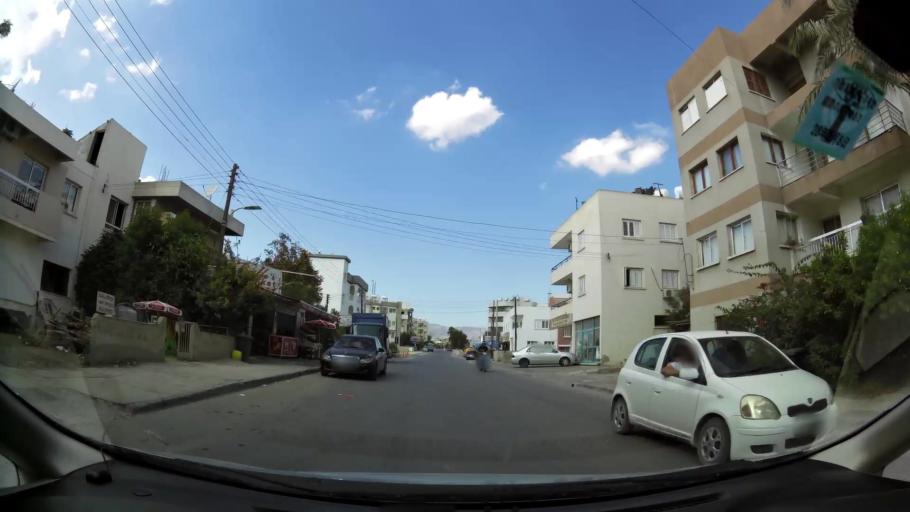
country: CY
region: Lefkosia
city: Nicosia
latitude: 35.2211
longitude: 33.3012
